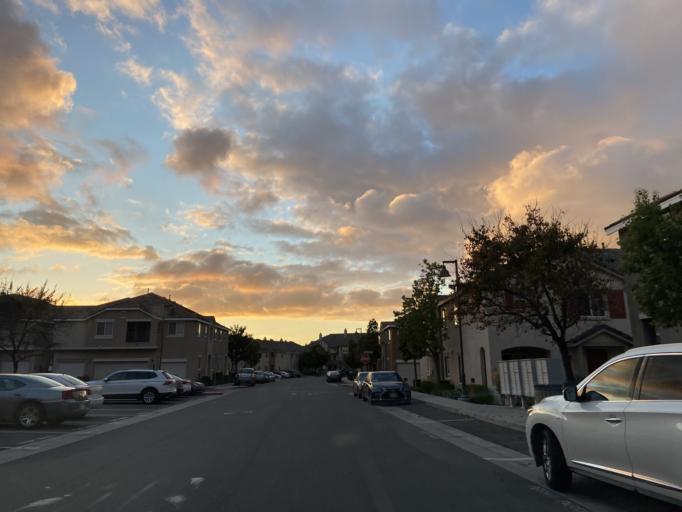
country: US
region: California
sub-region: San Diego County
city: Bonita
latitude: 32.6273
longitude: -116.9725
